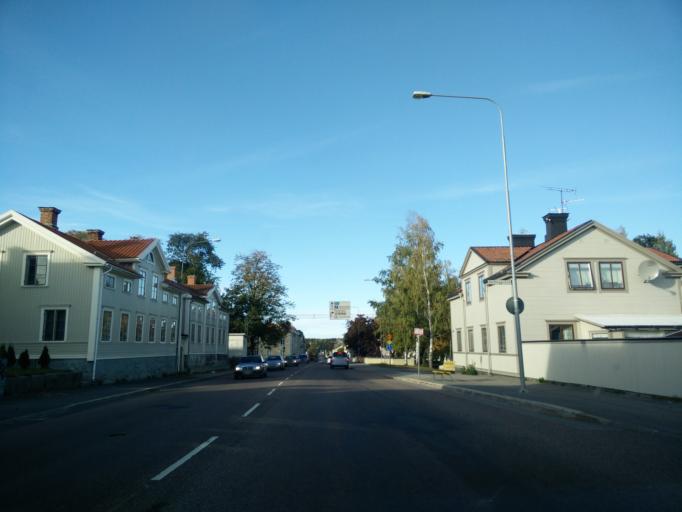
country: SE
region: Gaevleborg
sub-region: Hudiksvalls Kommun
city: Hudiksvall
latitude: 61.7250
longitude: 17.1024
